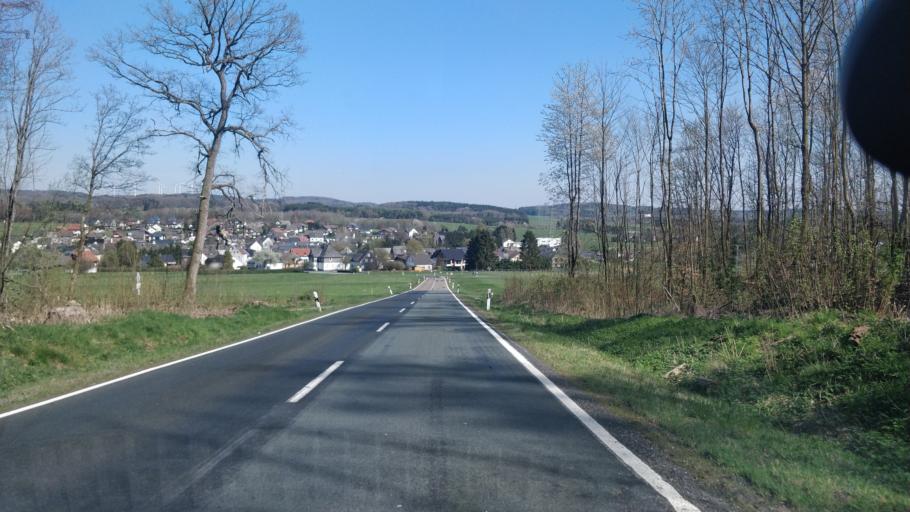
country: DE
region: Rheinland-Pfalz
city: Niederrossbach
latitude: 50.6398
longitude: 8.0256
